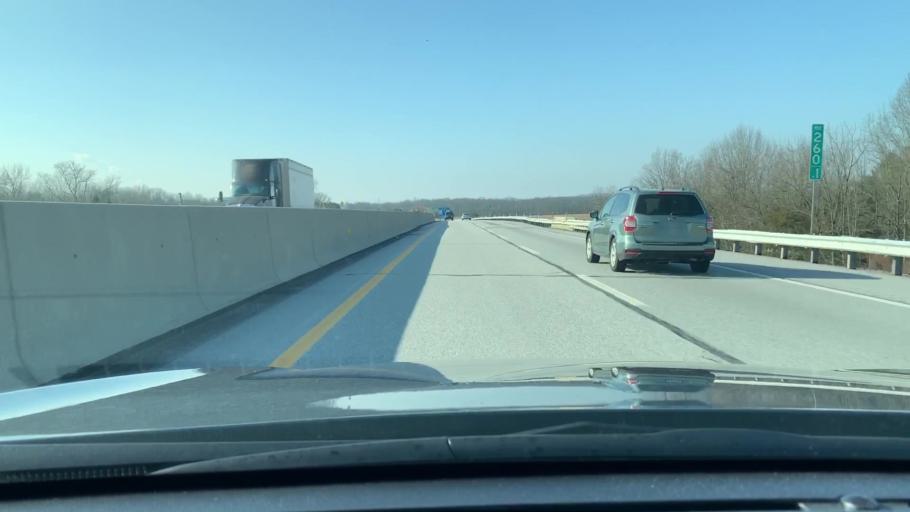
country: US
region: Pennsylvania
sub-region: Lebanon County
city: Campbelltown
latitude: 40.2103
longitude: -76.5495
